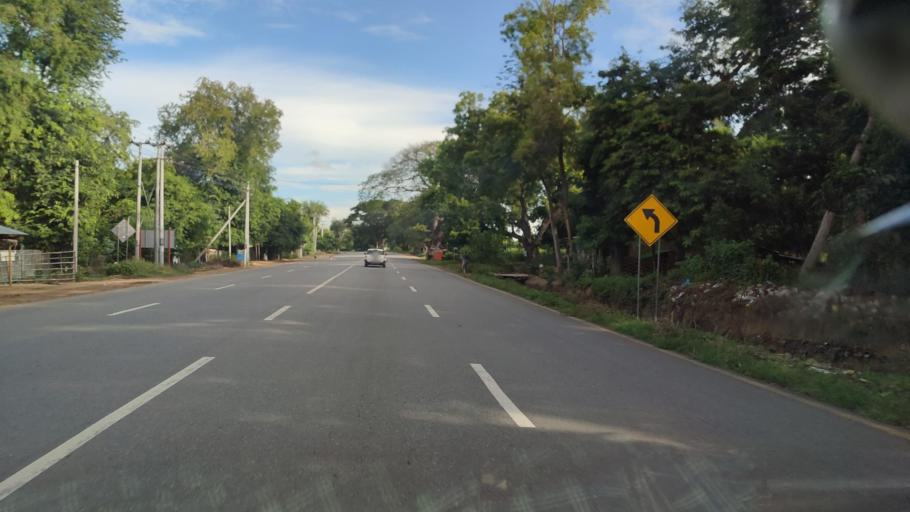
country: MM
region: Mandalay
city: Yamethin
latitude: 20.1888
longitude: 96.1855
